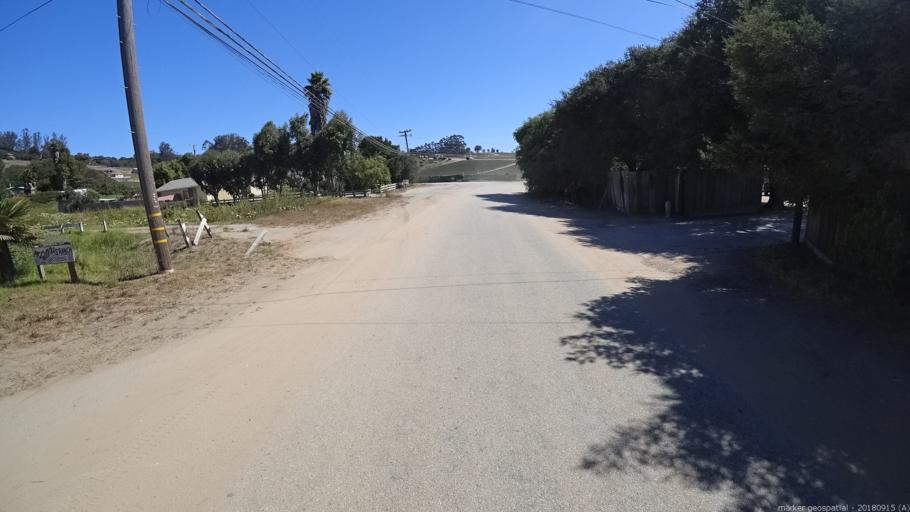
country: US
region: California
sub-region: Monterey County
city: Las Lomas
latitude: 36.8650
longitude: -121.7144
